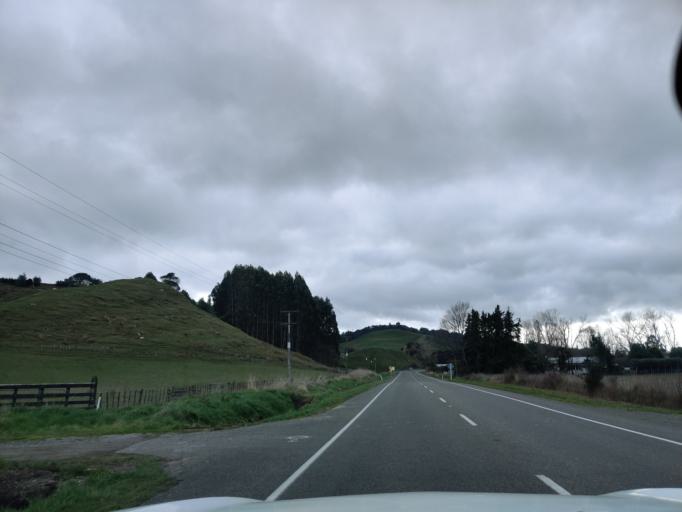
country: NZ
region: Manawatu-Wanganui
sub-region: Rangitikei District
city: Bulls
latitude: -39.9314
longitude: 175.5761
